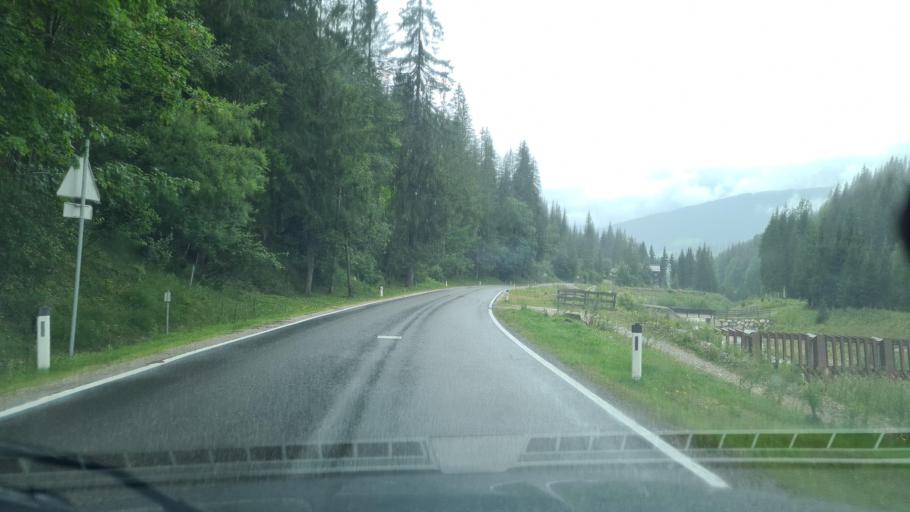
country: AT
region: Salzburg
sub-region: Politischer Bezirk Sankt Johann im Pongau
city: Altenmarkt im Pongau
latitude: 47.3487
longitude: 13.4281
